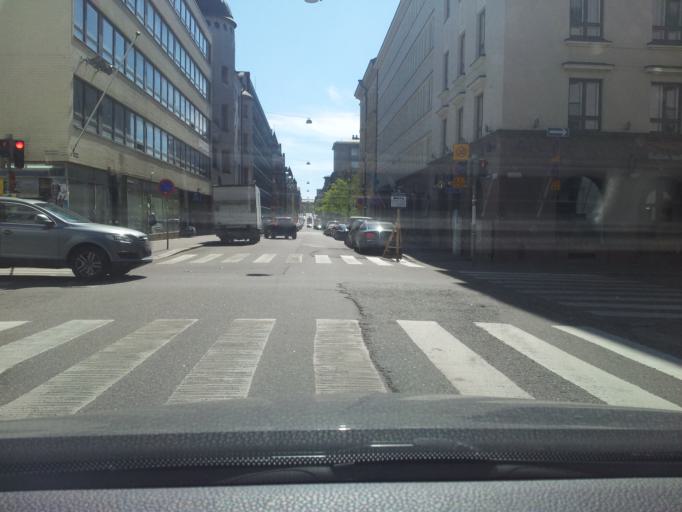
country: FI
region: Uusimaa
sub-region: Helsinki
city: Helsinki
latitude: 60.1646
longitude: 24.9329
